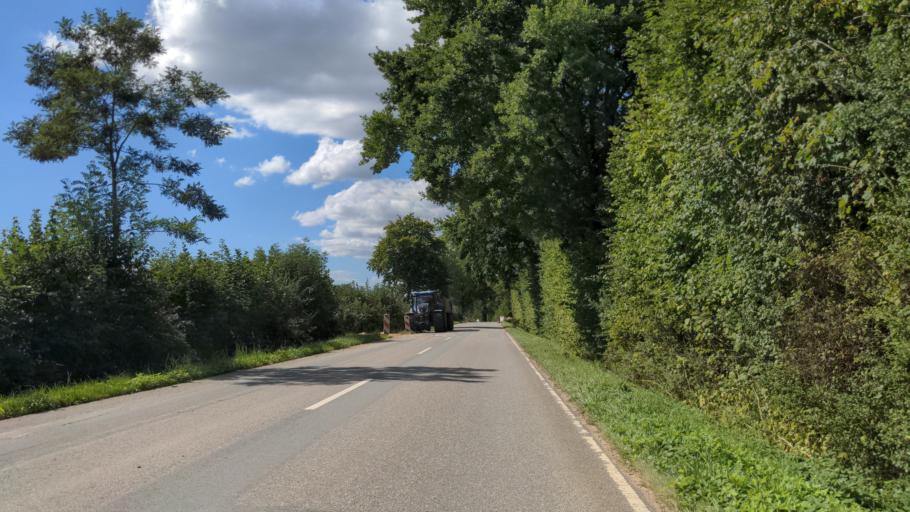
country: DE
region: Schleswig-Holstein
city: Beschendorf
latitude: 54.1988
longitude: 10.8174
